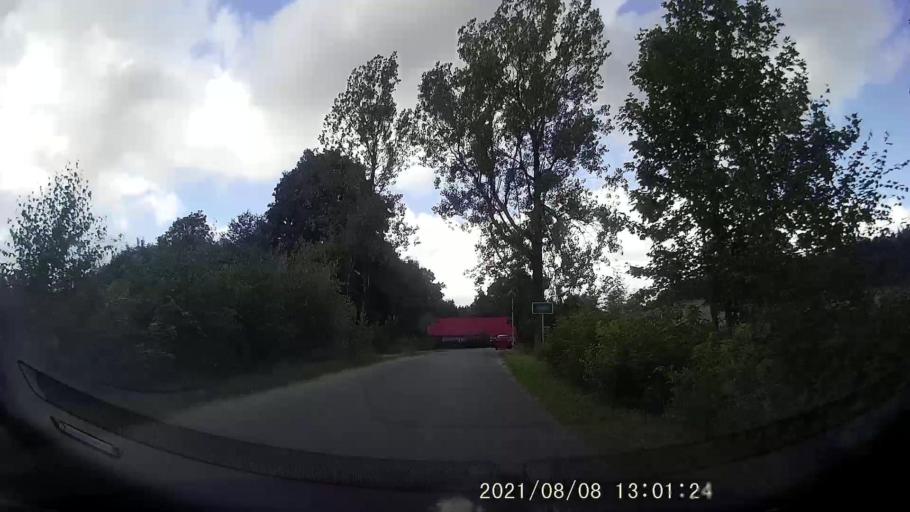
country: PL
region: Lower Silesian Voivodeship
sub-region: Powiat klodzki
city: Lewin Klodzki
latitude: 50.4199
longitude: 16.3393
